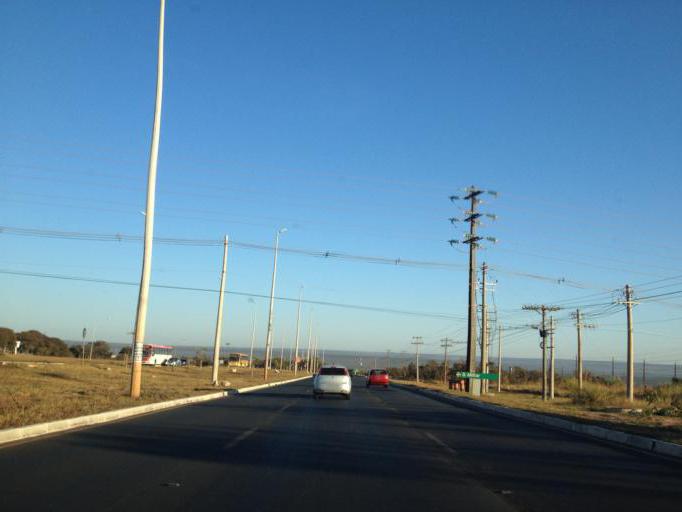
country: BR
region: Federal District
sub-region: Brasilia
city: Brasilia
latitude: -15.7607
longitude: -47.9219
